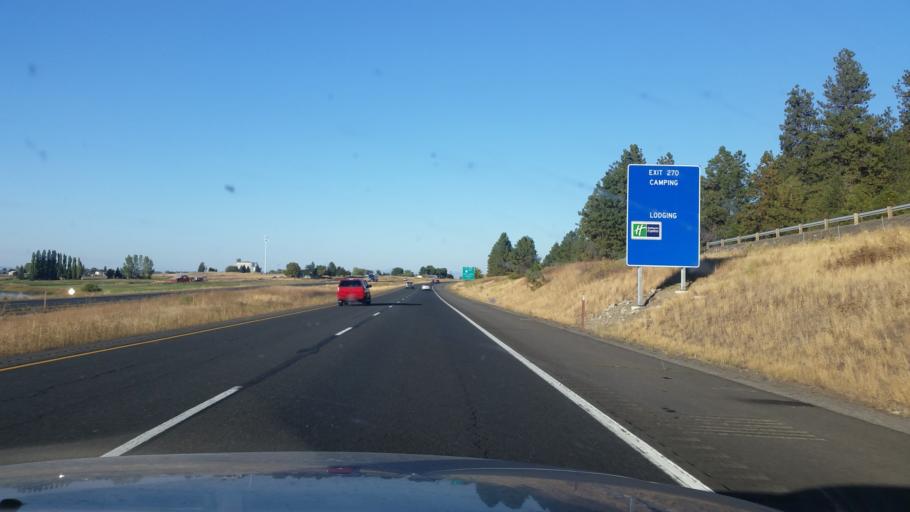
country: US
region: Washington
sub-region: Spokane County
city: Medical Lake
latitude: 47.5540
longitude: -117.6171
